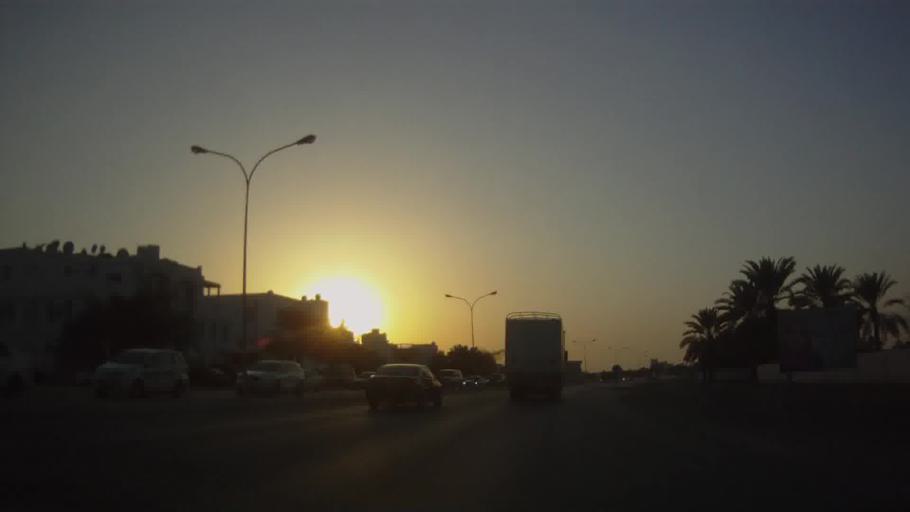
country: OM
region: Muhafazat Masqat
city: Bawshar
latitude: 23.5975
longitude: 58.3999
